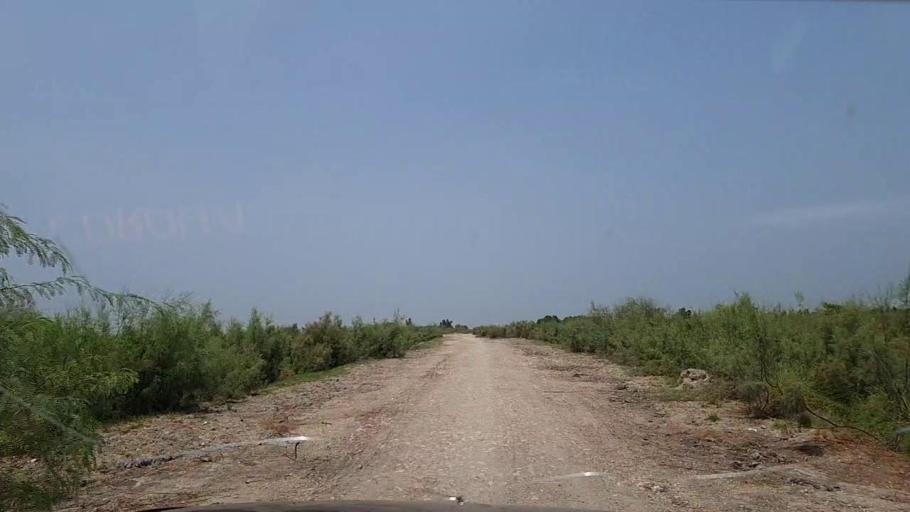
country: PK
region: Sindh
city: Adilpur
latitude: 27.8992
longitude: 69.2349
